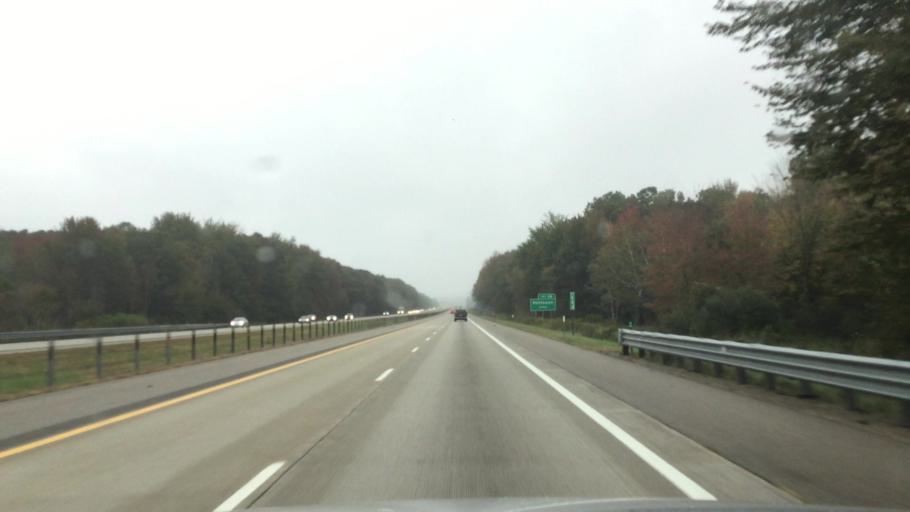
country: US
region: Michigan
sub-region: Van Buren County
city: Mattawan
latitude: 42.2206
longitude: -85.8139
